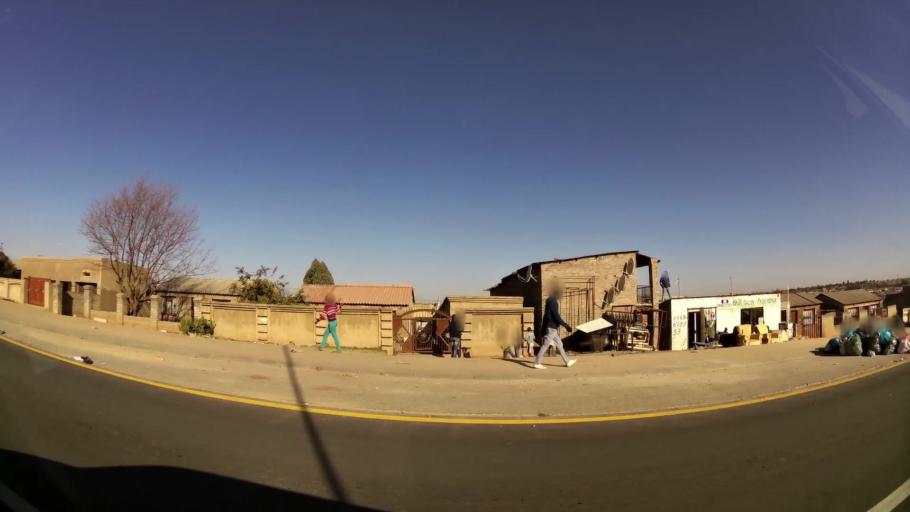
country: ZA
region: Gauteng
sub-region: Ekurhuleni Metropolitan Municipality
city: Tembisa
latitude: -26.0278
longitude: 28.2164
